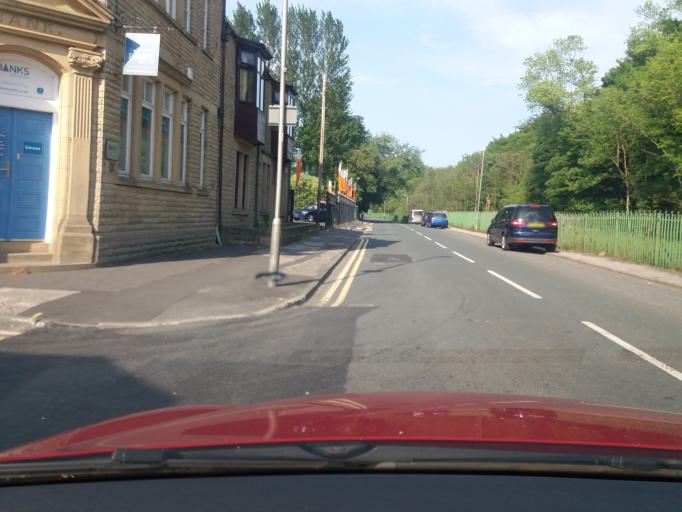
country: GB
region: England
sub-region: Lancashire
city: Chorley
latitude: 53.6907
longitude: -2.5598
